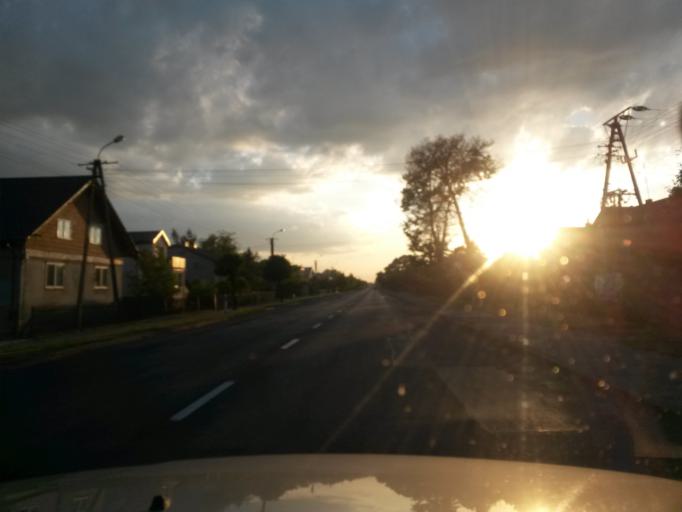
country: PL
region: Lodz Voivodeship
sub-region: Powiat wielunski
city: Mokrsko
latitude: 51.2610
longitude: 18.4775
